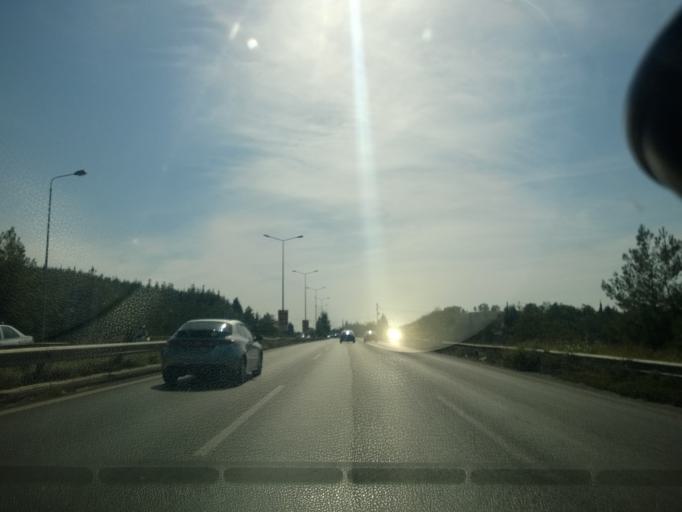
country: GR
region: Central Macedonia
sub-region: Nomos Thessalonikis
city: Agios Pavlos
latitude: 40.6574
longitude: 22.9673
